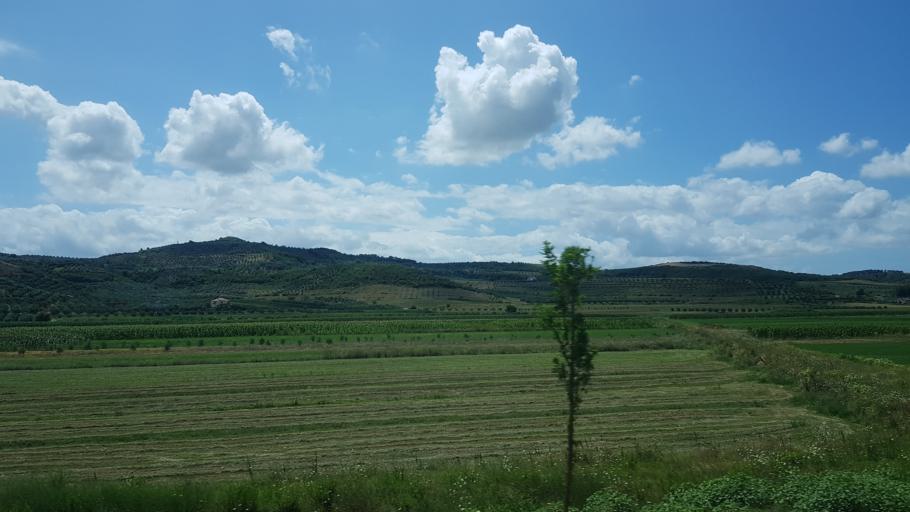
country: AL
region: Fier
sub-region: Rrethi i Fierit
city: Cakran
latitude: 40.5954
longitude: 19.5923
